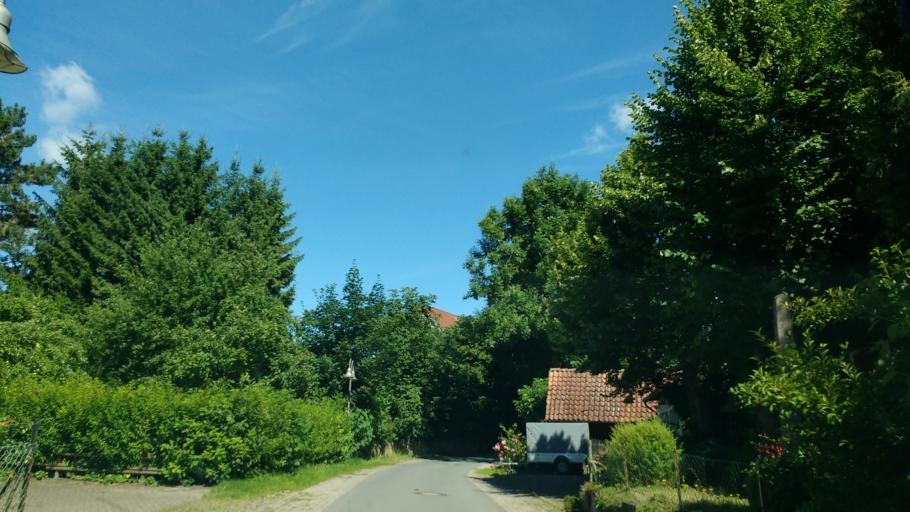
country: DE
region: North Rhine-Westphalia
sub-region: Regierungsbezirk Detmold
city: Dorentrup
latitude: 52.0217
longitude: 9.0562
